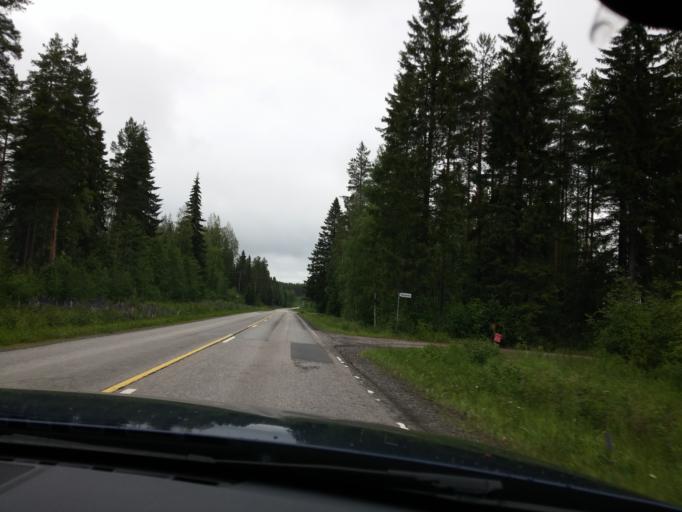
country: FI
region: Central Finland
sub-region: Keuruu
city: Keuruu
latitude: 62.3269
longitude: 24.7334
